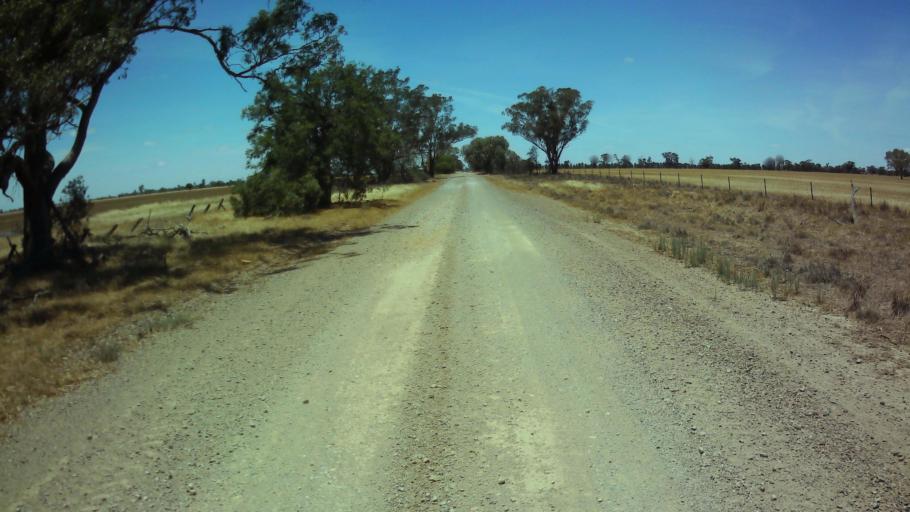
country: AU
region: New South Wales
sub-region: Weddin
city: Grenfell
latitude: -33.9435
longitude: 147.7113
